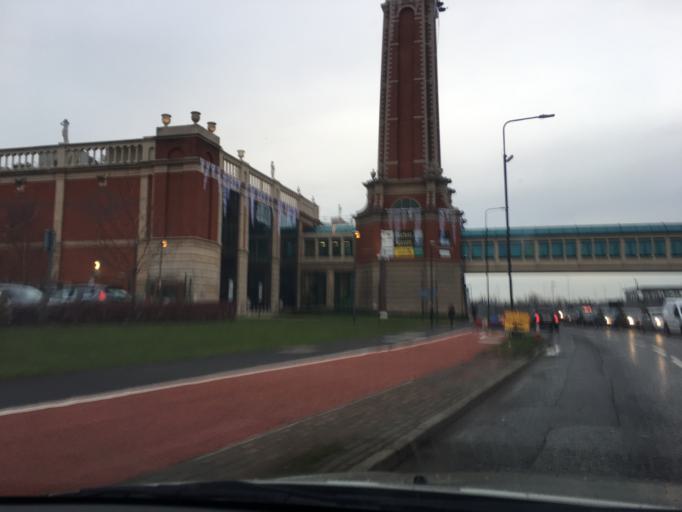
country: GB
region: England
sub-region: City and Borough of Salford
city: Eccles
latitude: 53.4665
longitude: -2.3439
